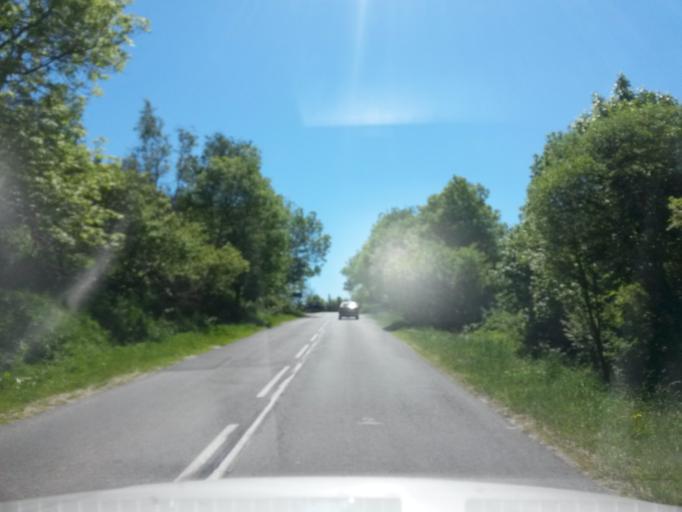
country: PL
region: Lower Silesian Voivodeship
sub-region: Powiat jeleniogorski
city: Kowary
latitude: 50.7636
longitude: 15.8661
